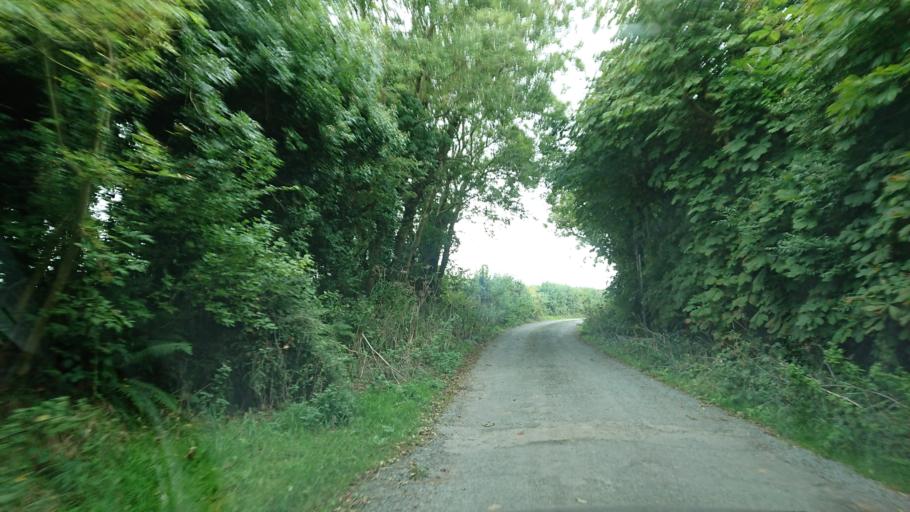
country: IE
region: Munster
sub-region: Waterford
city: Dunmore East
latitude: 52.2036
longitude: -7.0453
